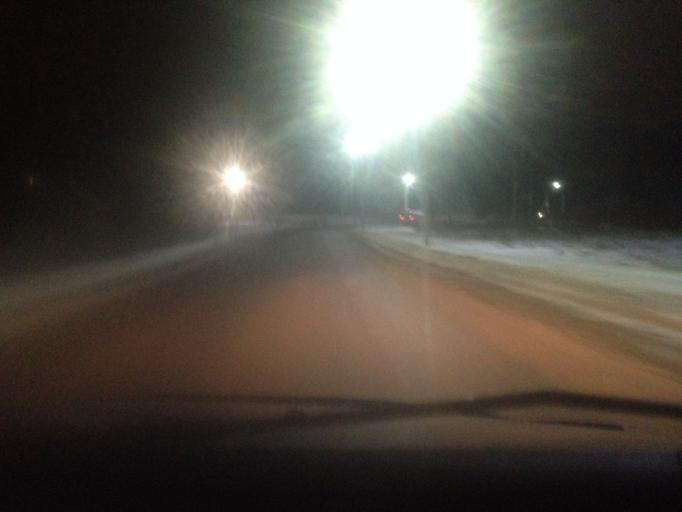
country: RU
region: Tula
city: Leninskiy
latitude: 54.2791
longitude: 37.4553
